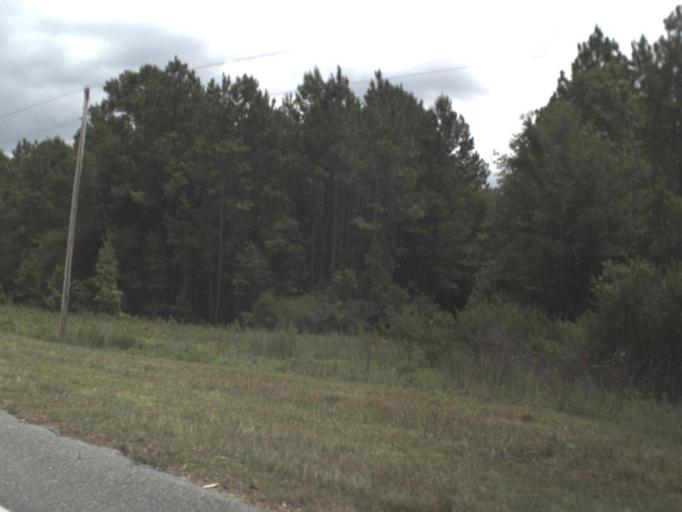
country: US
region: Florida
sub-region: Taylor County
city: Perry
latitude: 30.0814
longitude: -83.5038
